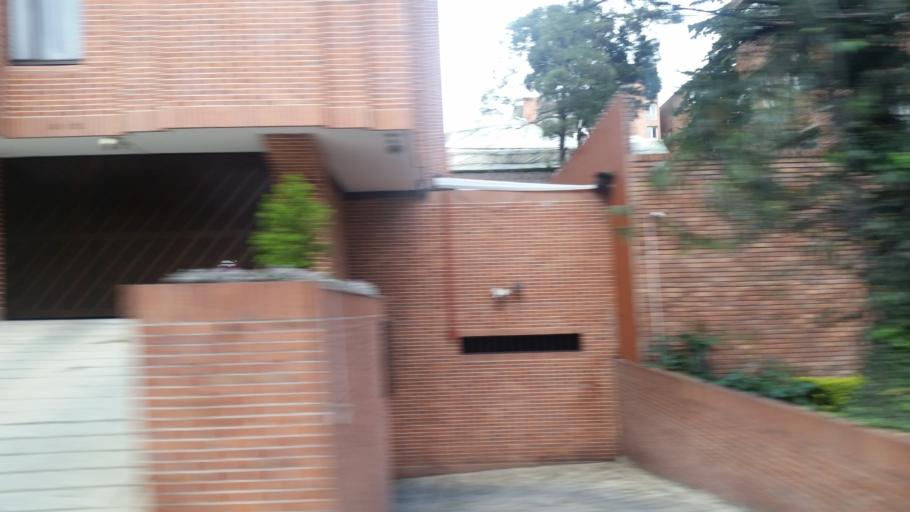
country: CO
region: Bogota D.C.
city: Barrio San Luis
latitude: 4.6533
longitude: -74.0555
